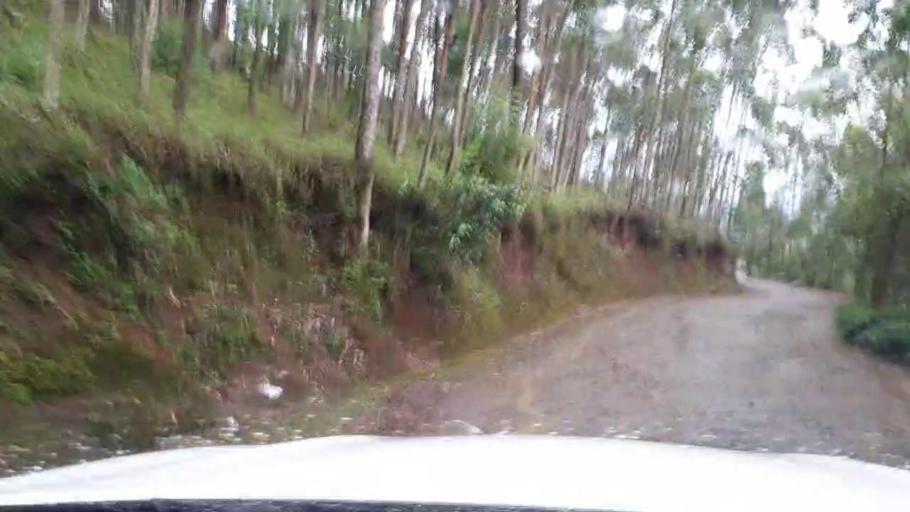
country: RW
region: Western Province
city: Cyangugu
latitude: -2.4707
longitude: 29.0316
